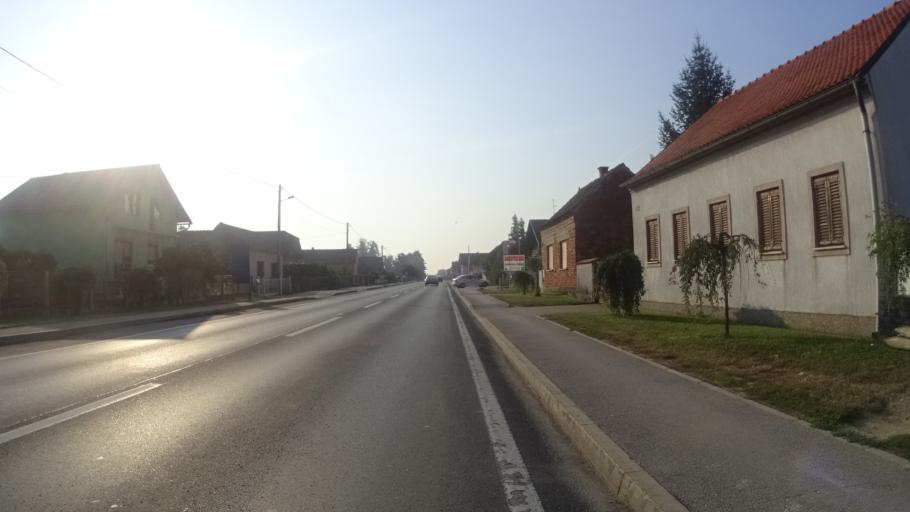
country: HR
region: Varazdinska
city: Sracinec
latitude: 46.3298
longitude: 16.2784
